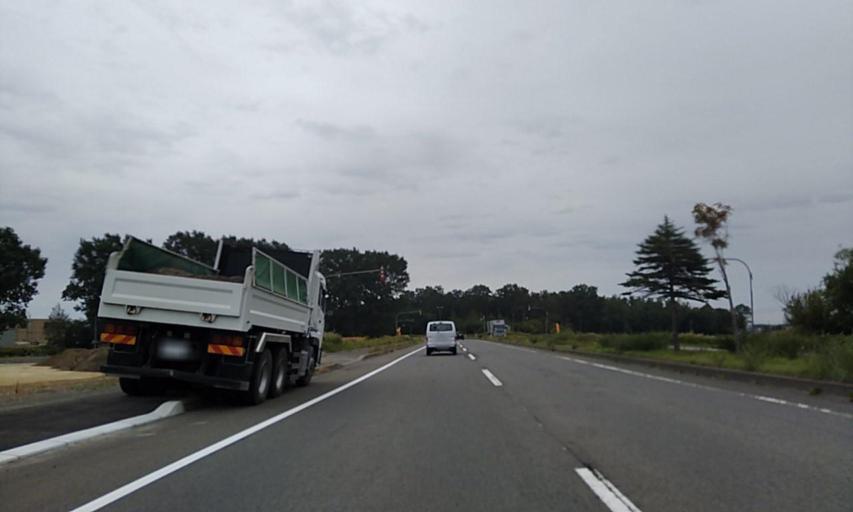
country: JP
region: Hokkaido
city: Ishikari
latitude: 43.1589
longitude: 141.2749
